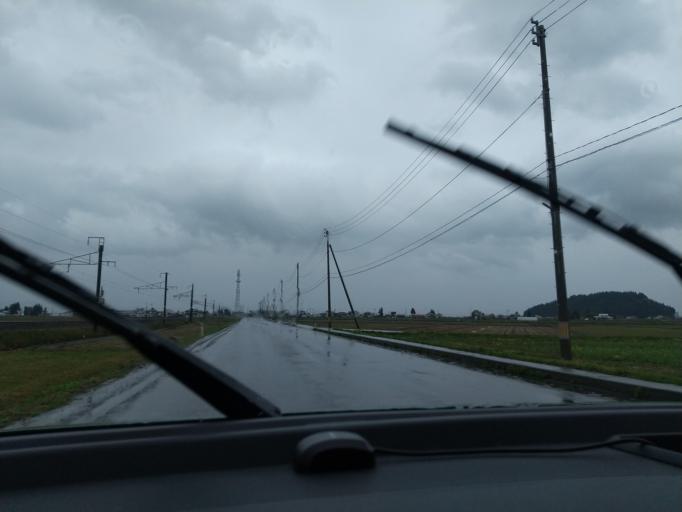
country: JP
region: Akita
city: Yokotemachi
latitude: 39.3686
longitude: 140.5366
